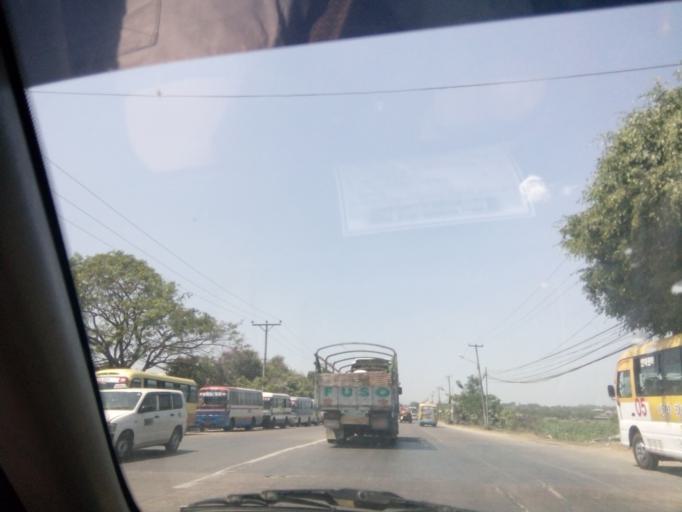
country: MM
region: Yangon
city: Yangon
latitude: 16.9343
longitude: 96.1485
